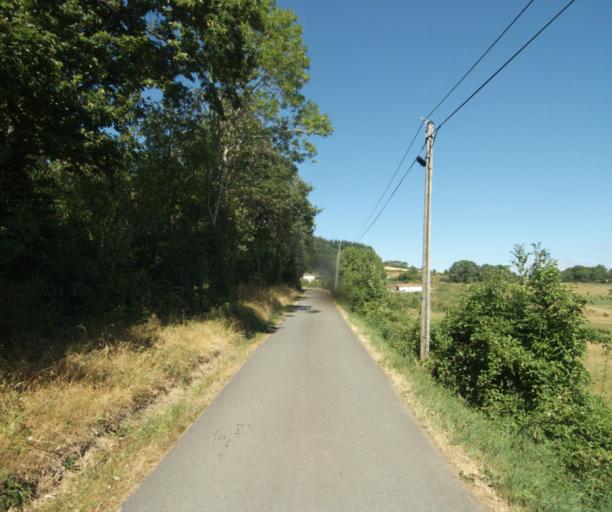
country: FR
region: Rhone-Alpes
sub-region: Departement du Rhone
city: Saint-Romain-de-Popey
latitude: 45.8110
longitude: 4.5098
